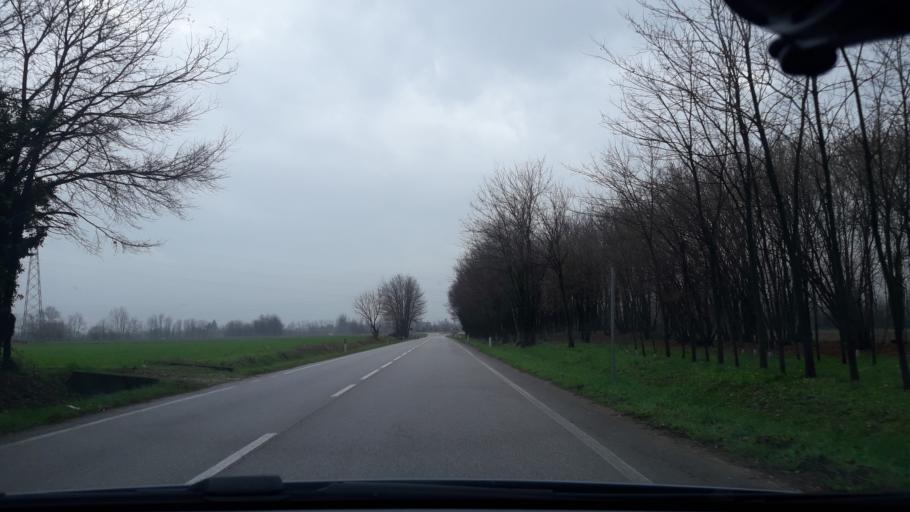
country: IT
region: Friuli Venezia Giulia
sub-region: Provincia di Udine
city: Colloredo di Prato
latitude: 46.0613
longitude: 13.1340
